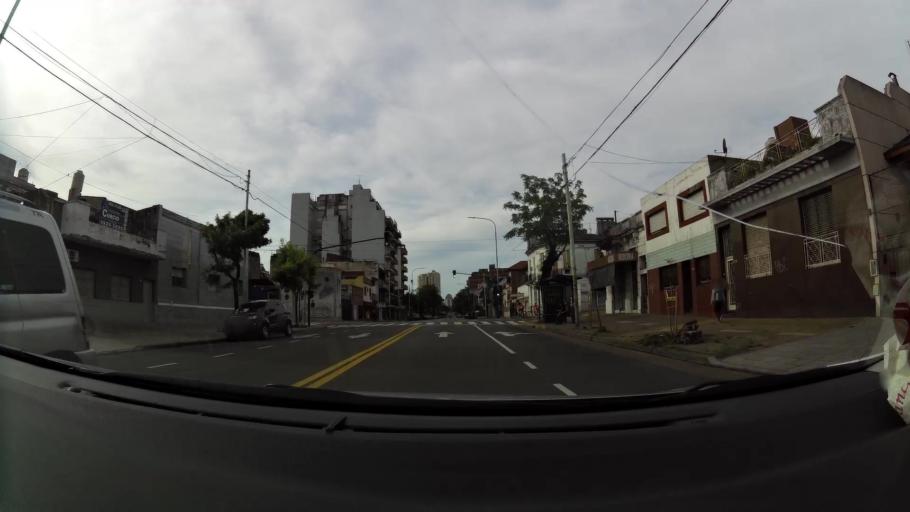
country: AR
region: Buenos Aires F.D.
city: Villa Lugano
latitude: -34.6398
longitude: -58.4315
